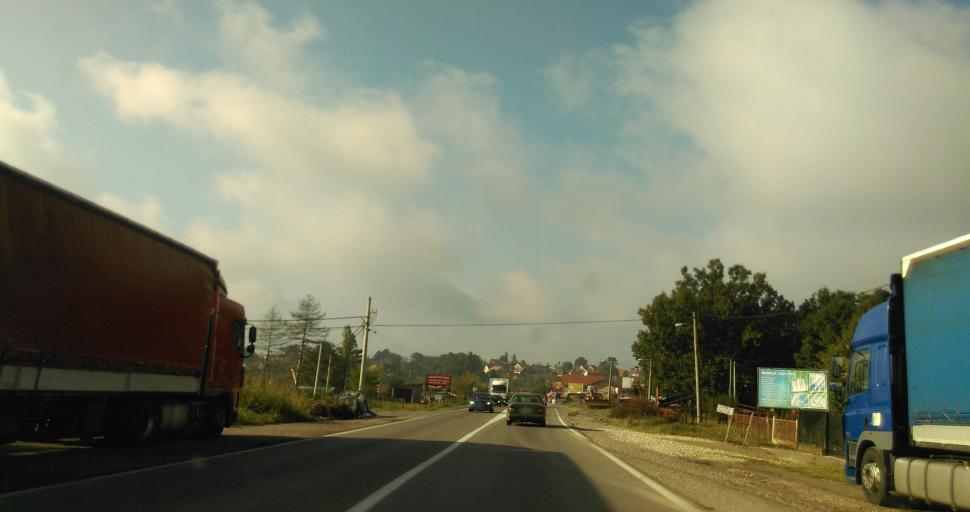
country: RS
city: Vranic
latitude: 44.6083
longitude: 20.3578
